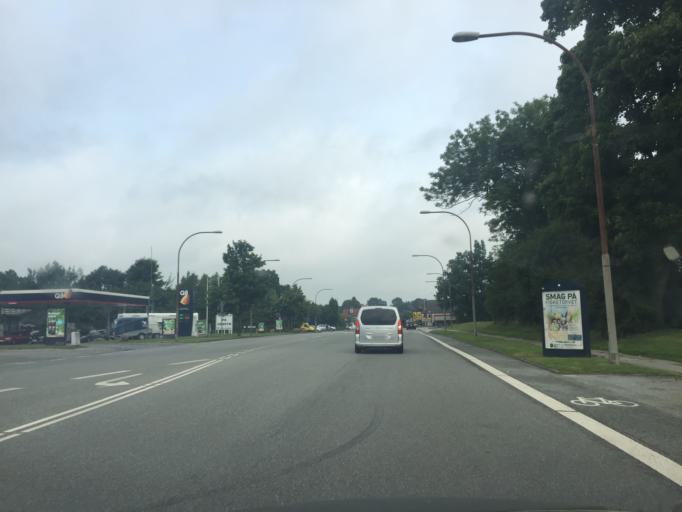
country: DK
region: Capital Region
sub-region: Herlev Kommune
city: Herlev
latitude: 55.7337
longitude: 12.4607
